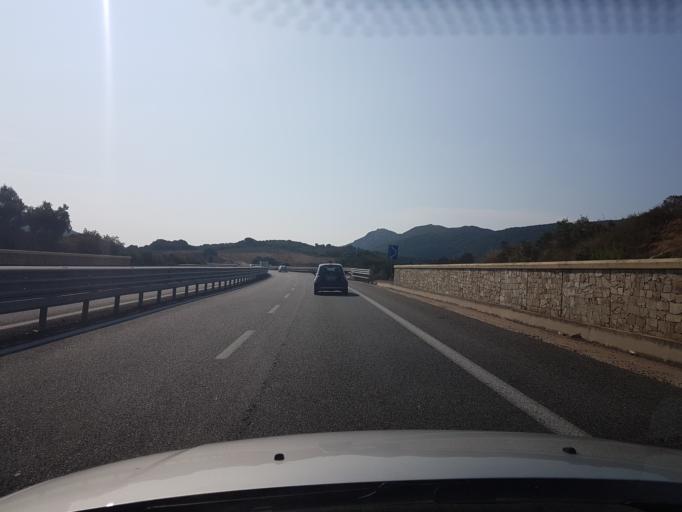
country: IT
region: Sardinia
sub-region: Provincia di Olbia-Tempio
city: San Teodoro
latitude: 40.7974
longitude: 9.5952
